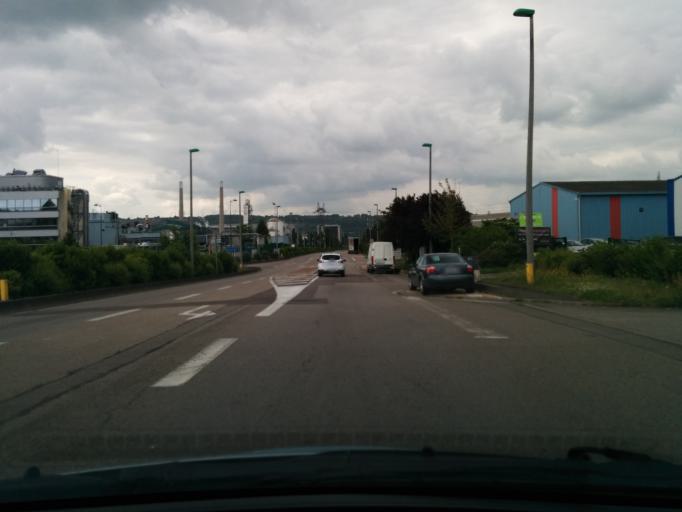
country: FR
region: Ile-de-France
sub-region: Departement des Yvelines
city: Limay
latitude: 48.9899
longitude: 1.7619
